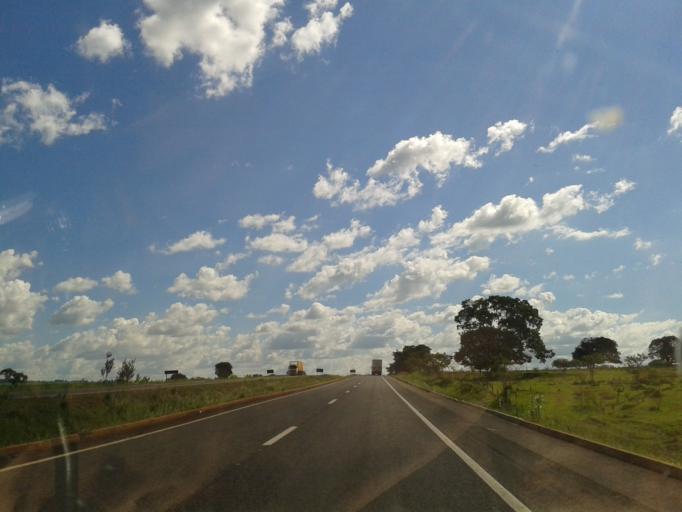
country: BR
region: Goias
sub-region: Morrinhos
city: Morrinhos
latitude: -17.7689
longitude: -49.1709
